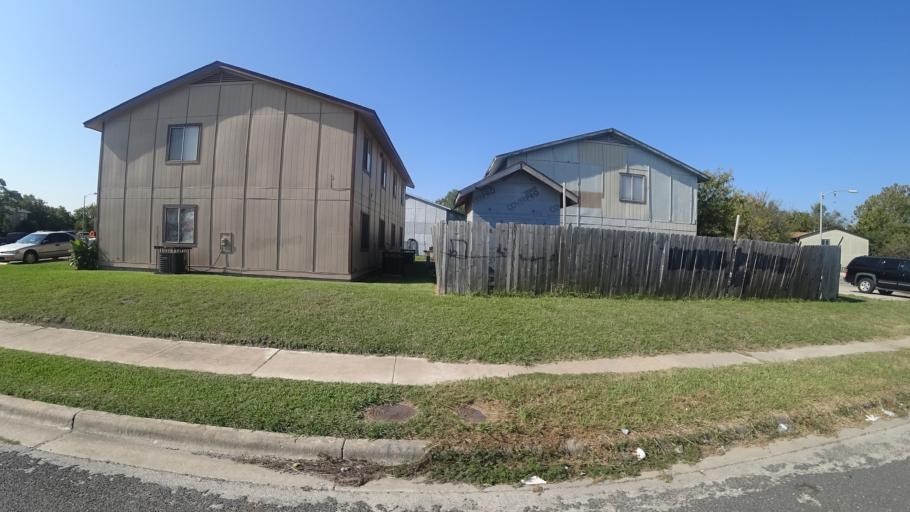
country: US
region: Texas
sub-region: Travis County
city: Austin
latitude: 30.3192
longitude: -97.6660
